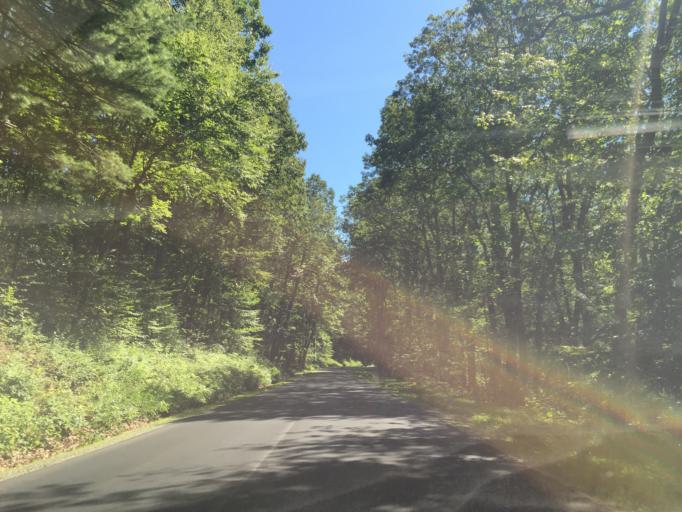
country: US
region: Virginia
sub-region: Page County
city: Luray
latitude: 38.6820
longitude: -78.3278
